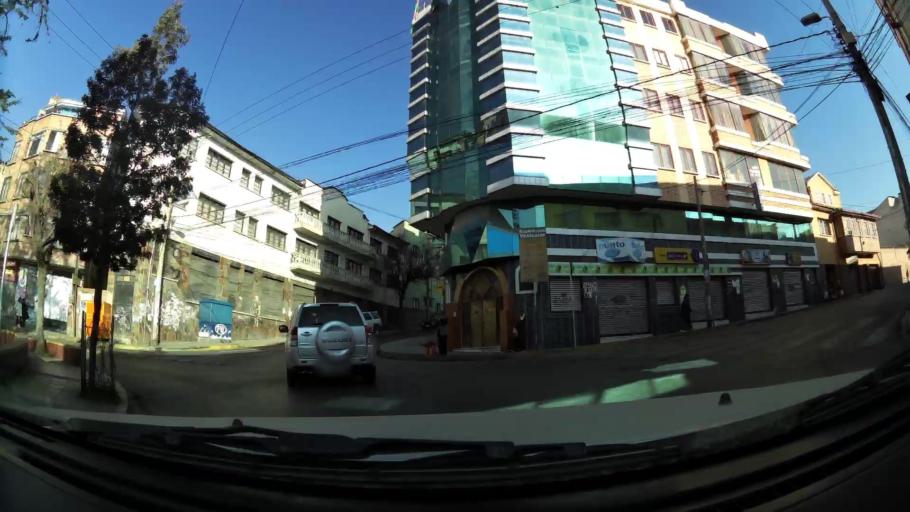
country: BO
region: La Paz
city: La Paz
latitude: -16.5041
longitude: -68.1408
